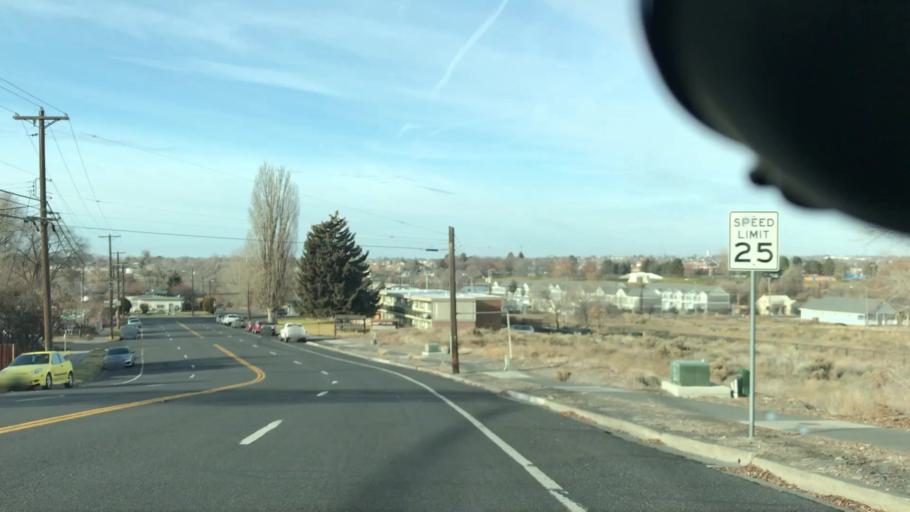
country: US
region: Washington
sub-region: Grant County
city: Moses Lake
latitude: 47.1215
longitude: -119.2718
